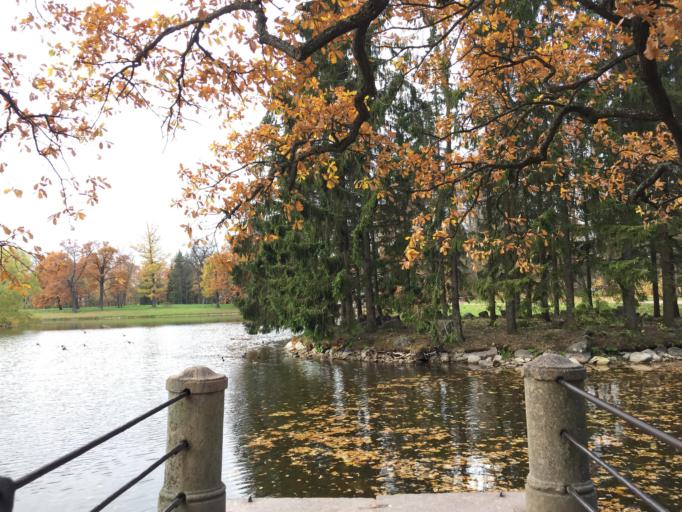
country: RU
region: St.-Petersburg
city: Pushkin
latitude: 59.7111
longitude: 30.3912
